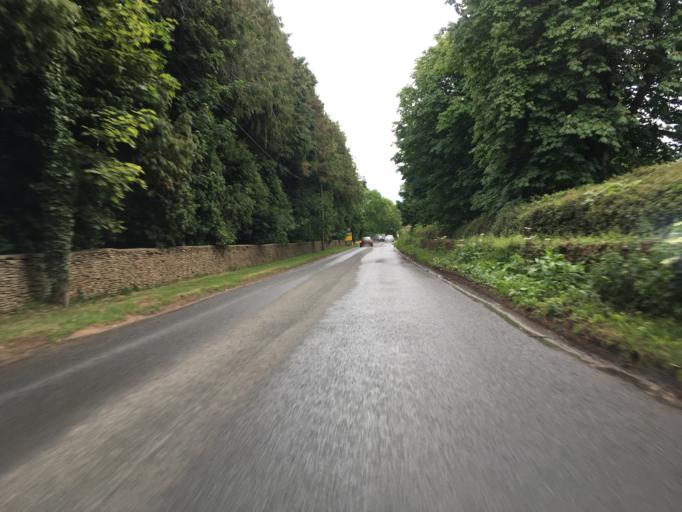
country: GB
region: England
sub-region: Gloucestershire
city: Tetbury
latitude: 51.6133
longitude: -2.2000
